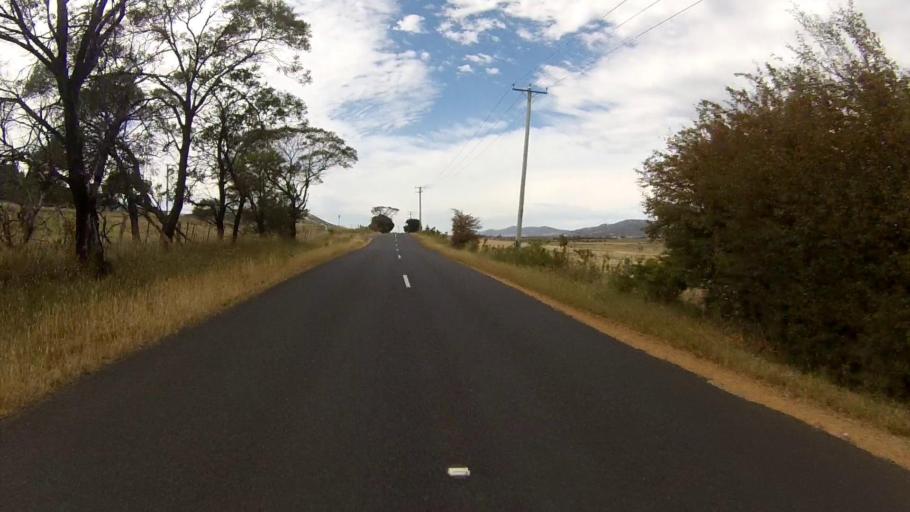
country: AU
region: Tasmania
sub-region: Clarence
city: Cambridge
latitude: -42.7266
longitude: 147.3987
